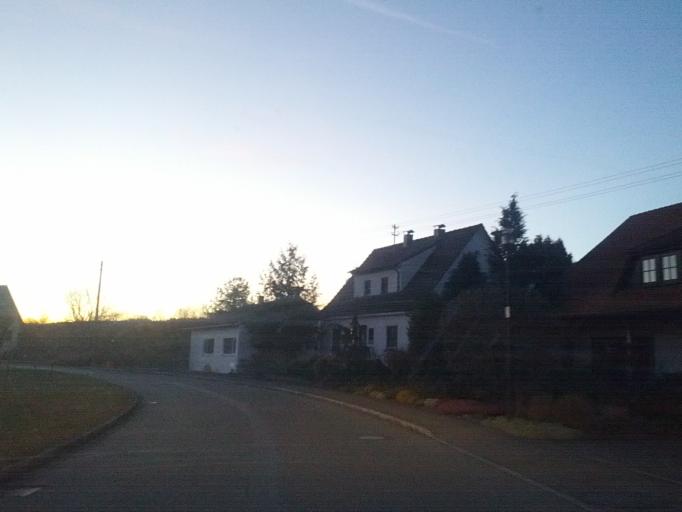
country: DE
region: Baden-Wuerttemberg
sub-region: Tuebingen Region
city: Rot an der Rot
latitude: 48.0170
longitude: 10.0304
